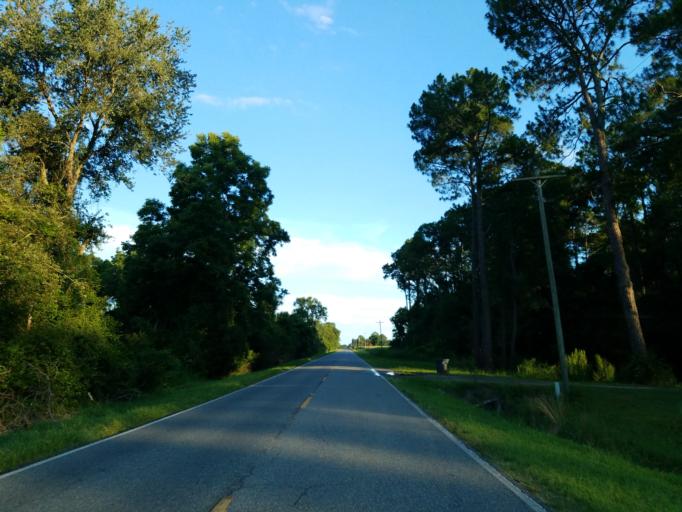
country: US
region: Georgia
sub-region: Tift County
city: Omega
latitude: 31.3046
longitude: -83.4727
